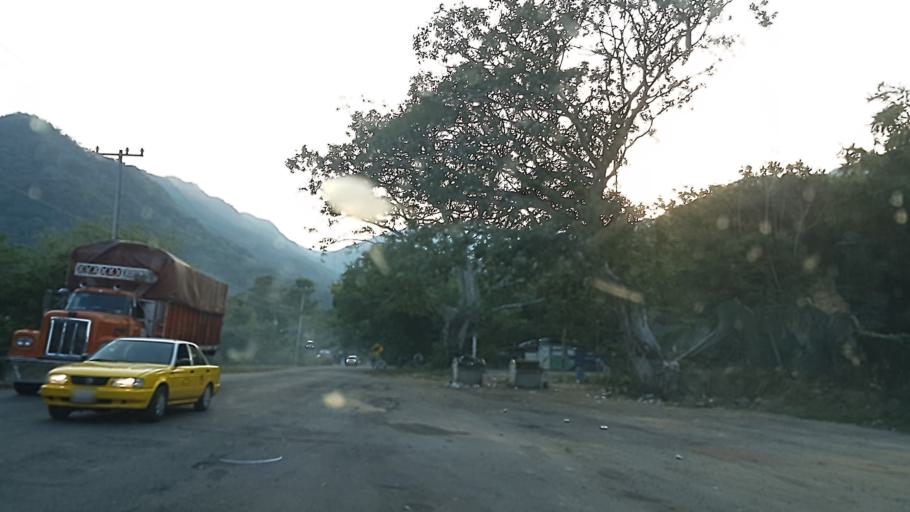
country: MX
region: Jalisco
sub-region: Puerto Vallarta
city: Puerto Vallarta
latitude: 20.5308
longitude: -105.2937
